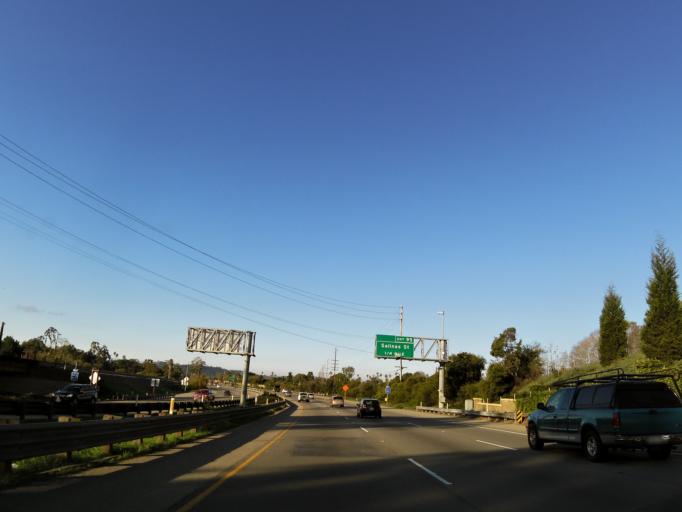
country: US
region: California
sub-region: Santa Barbara County
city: Montecito
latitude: 34.4232
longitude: -119.6584
